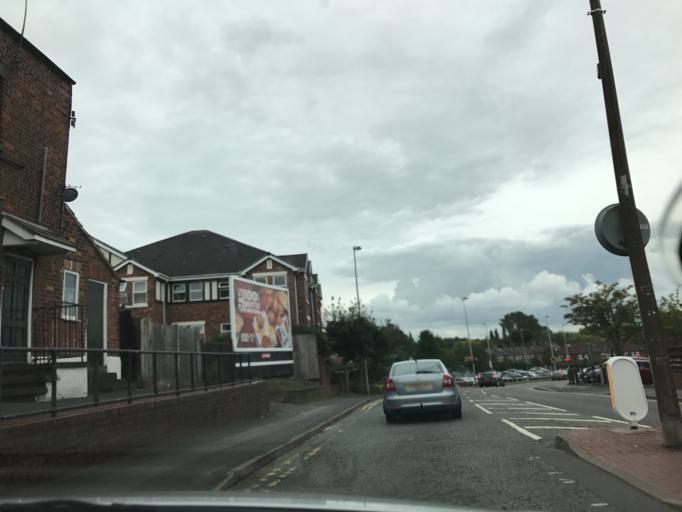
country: GB
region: England
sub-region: Cheshire West and Chester
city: Marston
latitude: 53.2624
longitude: -2.5076
